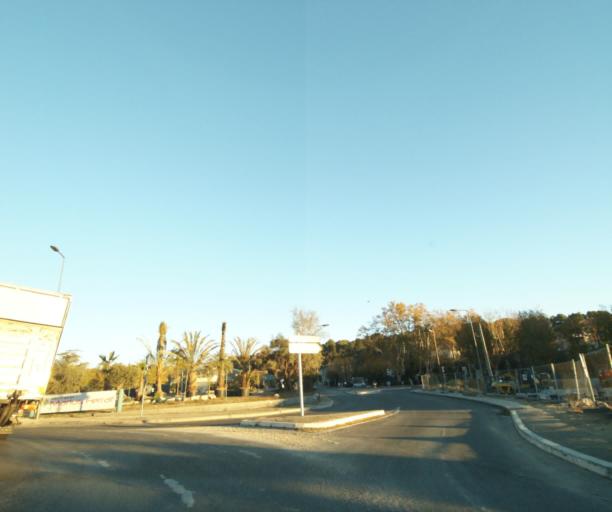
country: FR
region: Provence-Alpes-Cote d'Azur
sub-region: Departement des Bouches-du-Rhone
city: Allauch
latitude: 43.3060
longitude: 5.4702
